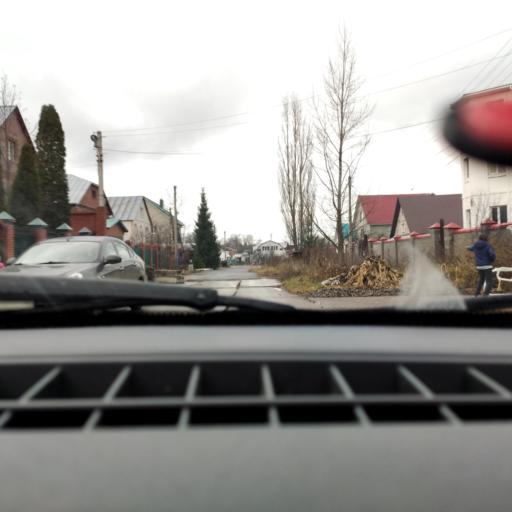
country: RU
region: Bashkortostan
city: Mikhaylovka
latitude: 54.7917
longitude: 55.9415
